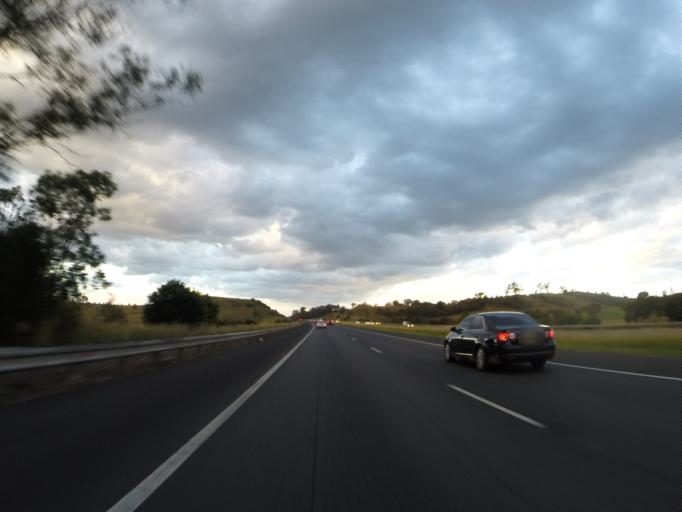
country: AU
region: New South Wales
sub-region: Campbelltown Municipality
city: Glen Alpine
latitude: -34.1182
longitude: 150.7573
